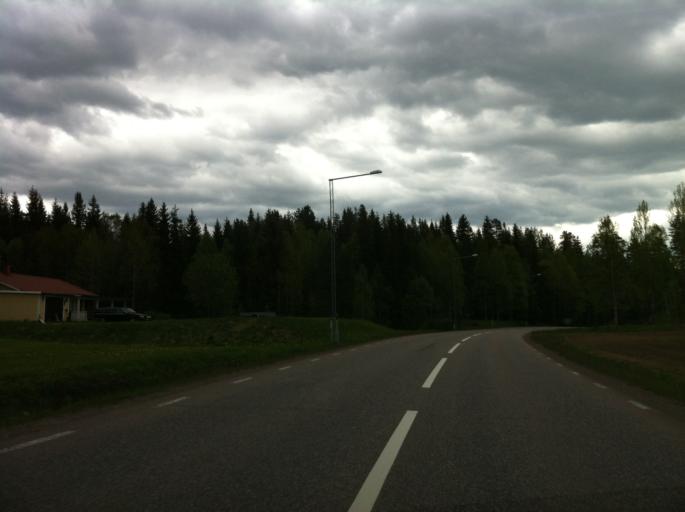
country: SE
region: Dalarna
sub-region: Malung-Saelens kommun
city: Malung
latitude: 61.1208
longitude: 13.2902
